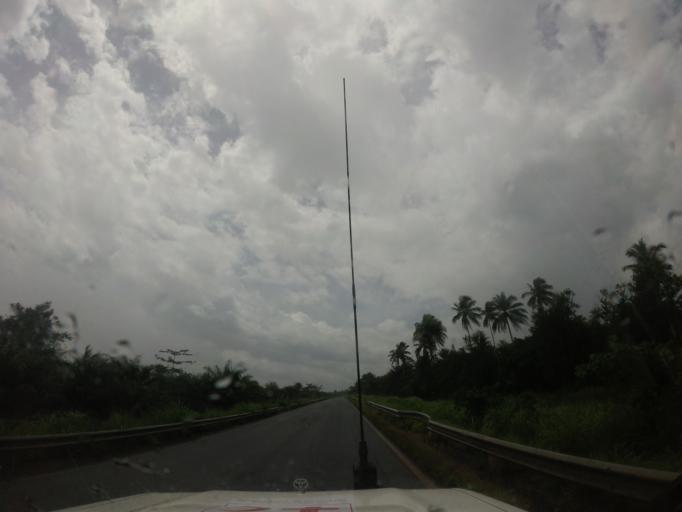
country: SL
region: Northern Province
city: Port Loko
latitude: 8.4865
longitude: -12.7880
